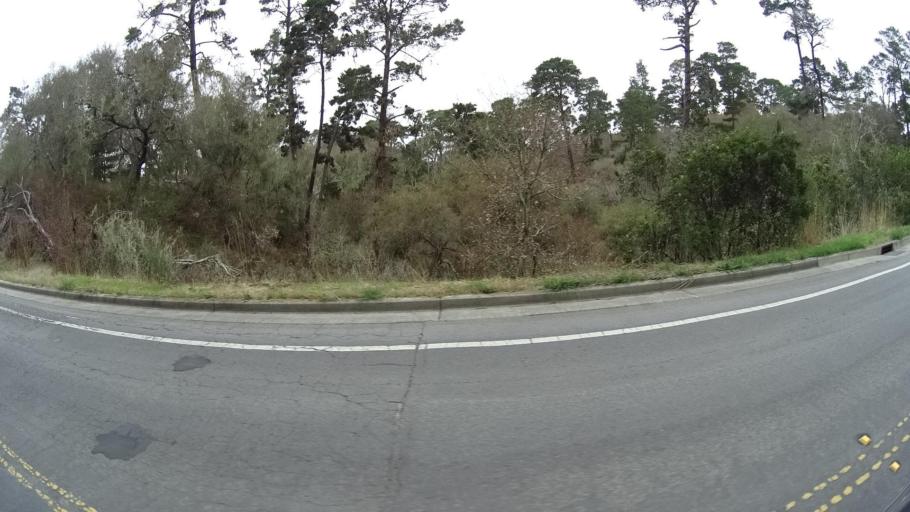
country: US
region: California
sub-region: Monterey County
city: Monterey
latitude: 36.5733
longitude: -121.8676
